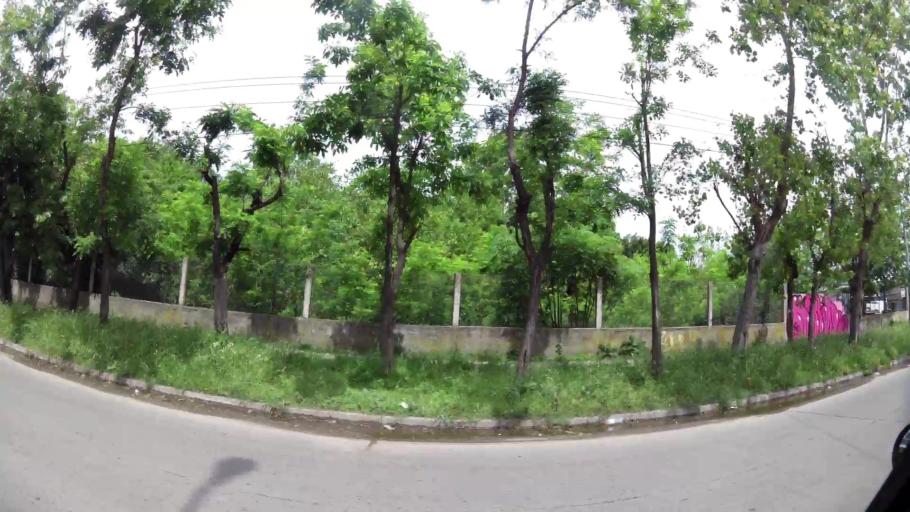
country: AR
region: Buenos Aires
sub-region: Partido de Quilmes
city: Quilmes
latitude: -34.7727
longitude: -58.2660
